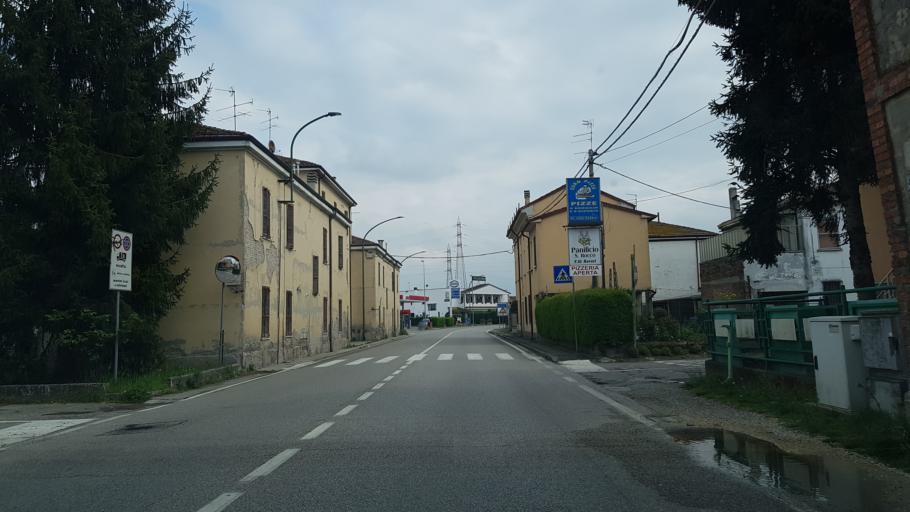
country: IT
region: Lombardy
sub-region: Provincia di Mantova
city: Ostiglia
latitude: 45.0681
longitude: 11.1399
